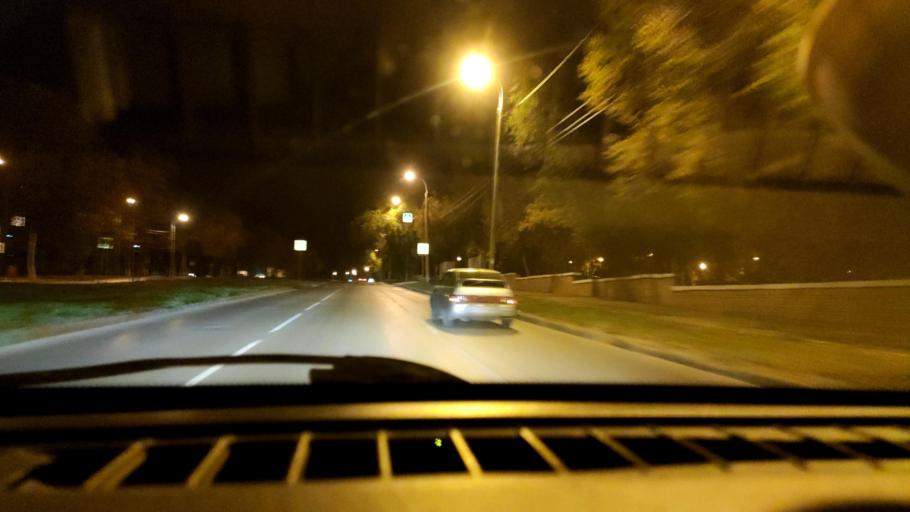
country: RU
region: Samara
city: Samara
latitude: 53.2206
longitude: 50.2388
